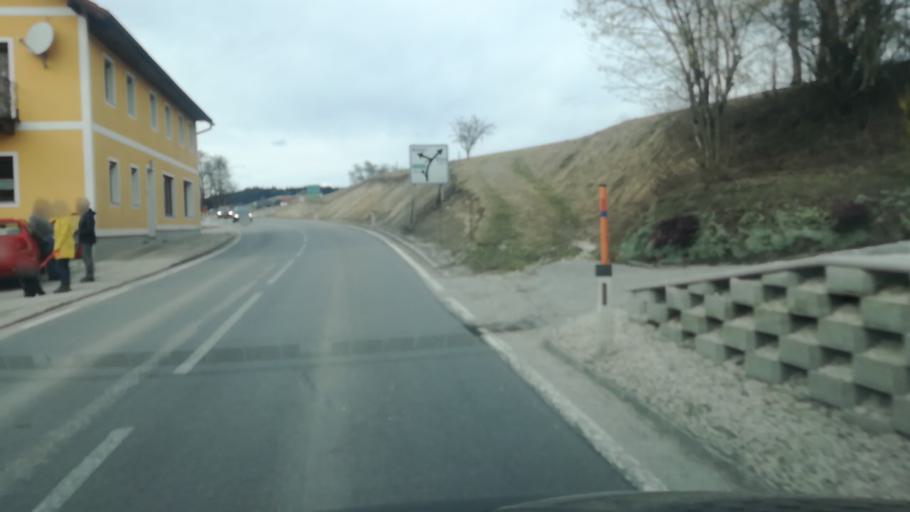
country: AT
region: Upper Austria
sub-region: Politischer Bezirk Vocklabruck
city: Frankenburg
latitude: 48.0827
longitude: 13.4833
